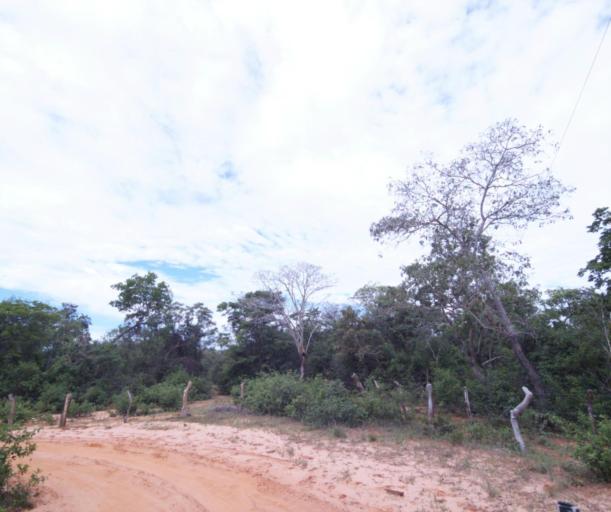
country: BR
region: Bahia
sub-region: Carinhanha
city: Carinhanha
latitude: -14.2378
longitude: -44.3817
